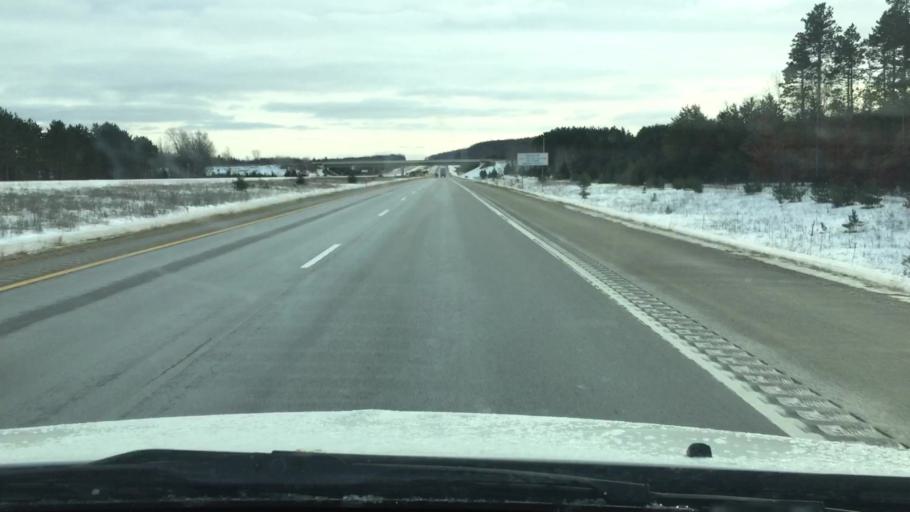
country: US
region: Michigan
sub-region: Wexford County
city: Manton
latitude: 44.4588
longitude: -85.3958
